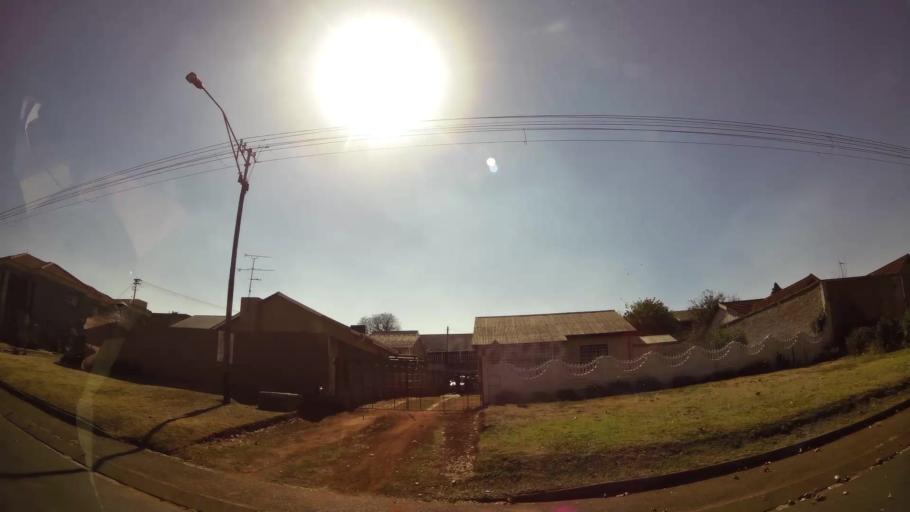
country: ZA
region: Gauteng
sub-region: City of Johannesburg Metropolitan Municipality
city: Roodepoort
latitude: -26.1893
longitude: 27.9506
